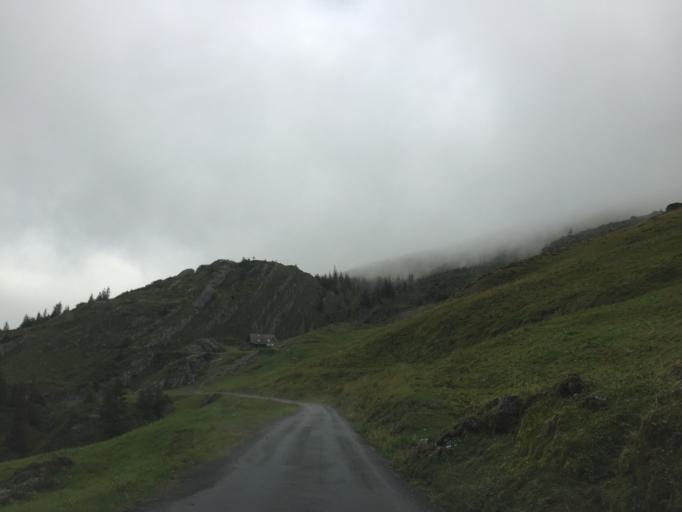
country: CH
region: Obwalden
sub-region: Obwalden
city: Sachseln
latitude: 46.7808
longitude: 8.2601
